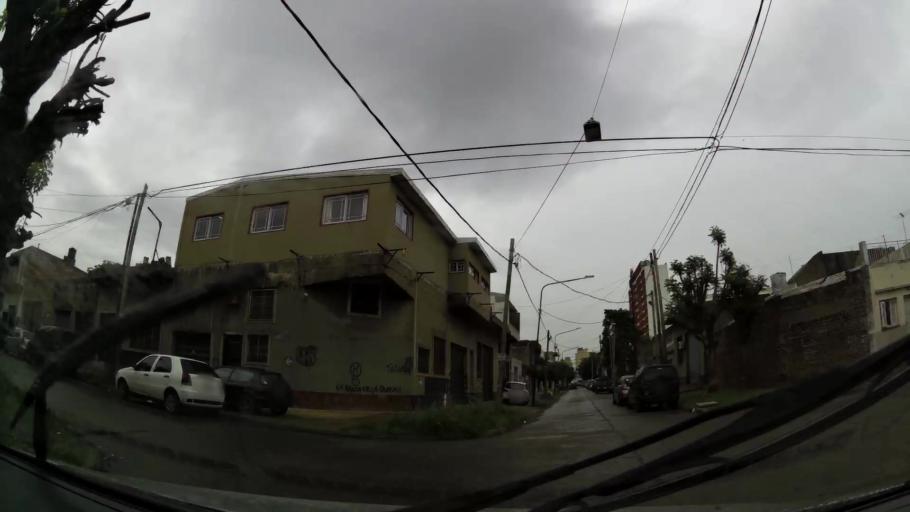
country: AR
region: Buenos Aires
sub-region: Partido de Lanus
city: Lanus
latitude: -34.6947
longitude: -58.3881
